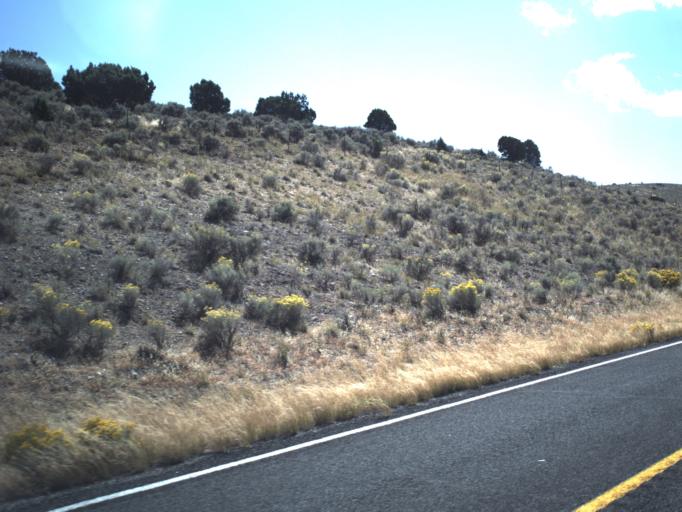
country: US
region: Utah
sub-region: Iron County
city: Parowan
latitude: 38.1018
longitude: -112.9488
